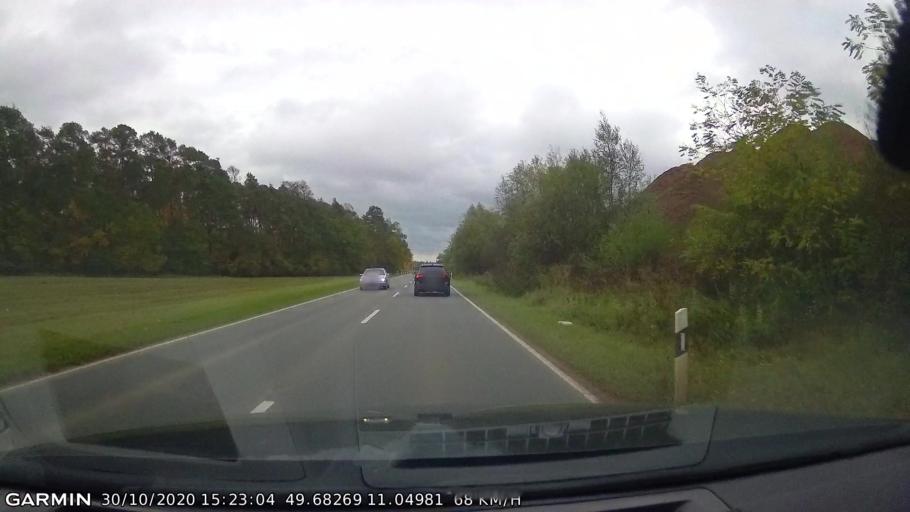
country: DE
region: Bavaria
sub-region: Upper Franconia
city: Hausen
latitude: 49.6827
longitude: 11.0498
